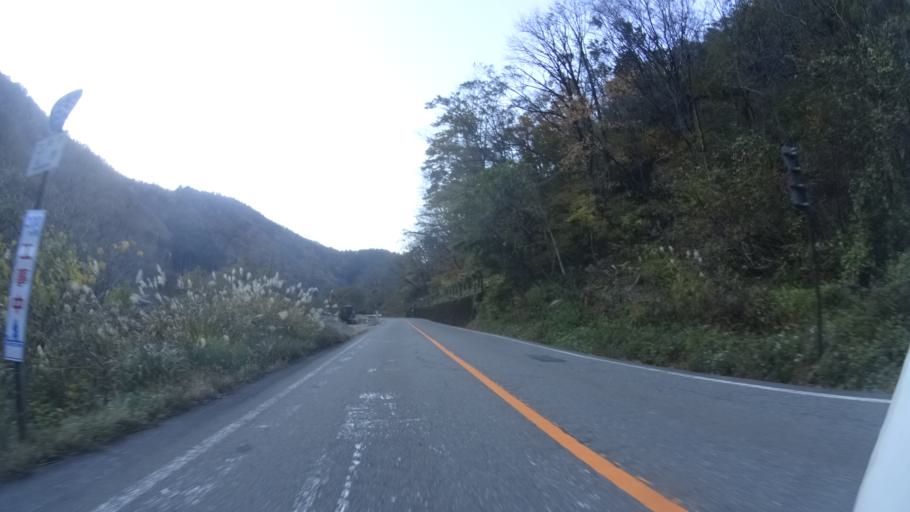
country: JP
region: Fukui
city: Ono
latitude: 35.9483
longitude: 136.6289
